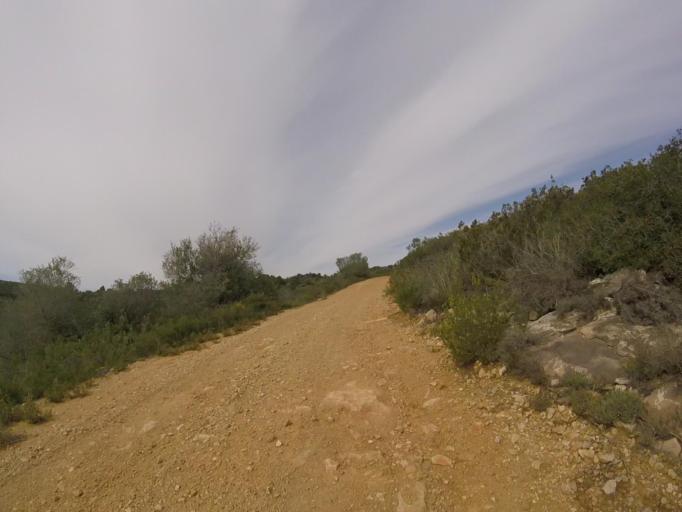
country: ES
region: Valencia
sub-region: Provincia de Castello
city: Cabanes
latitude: 40.1926
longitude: 0.1056
